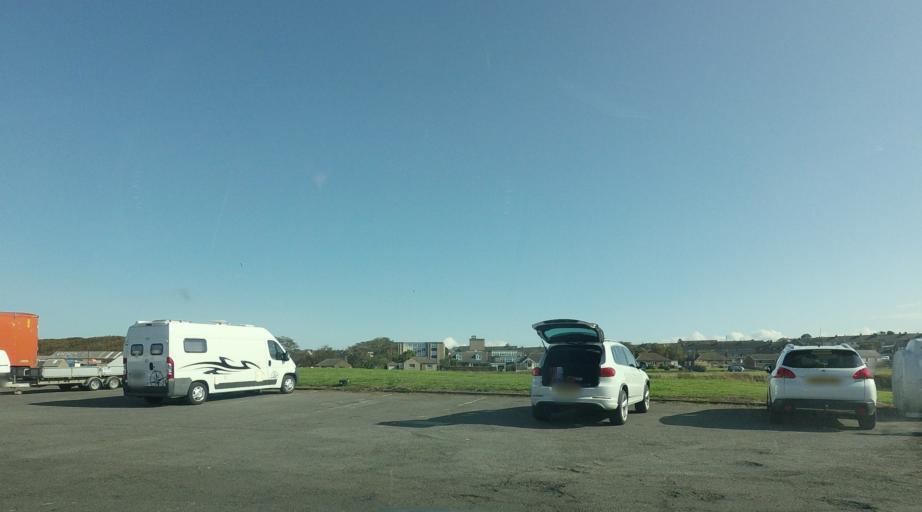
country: GB
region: Scotland
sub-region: Highland
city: Thurso
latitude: 58.5948
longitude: -3.5157
